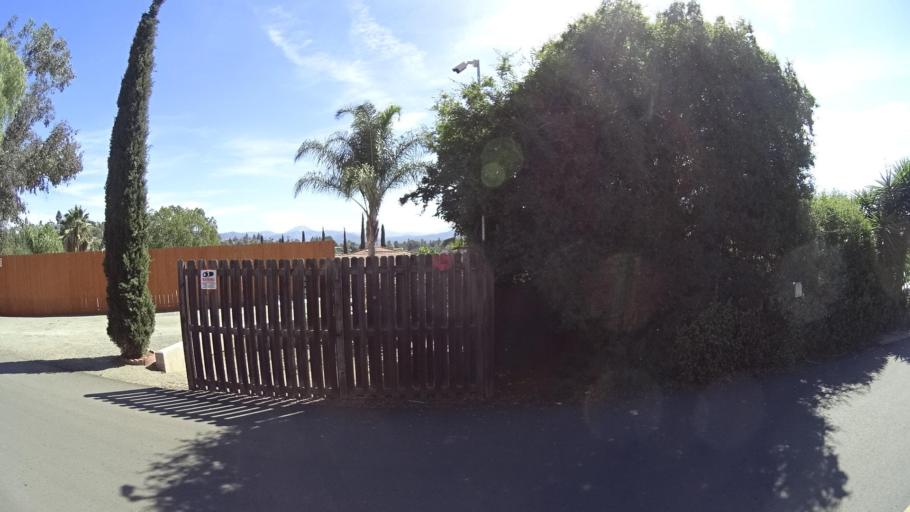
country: US
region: California
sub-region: San Diego County
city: Casa de Oro-Mount Helix
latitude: 32.7586
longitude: -116.9644
